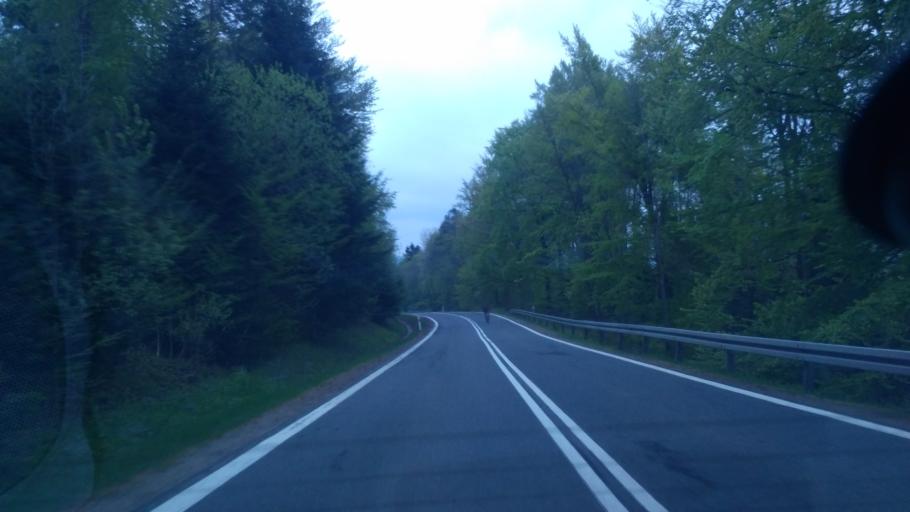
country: PL
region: Subcarpathian Voivodeship
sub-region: Powiat sanocki
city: Tyrawa Woloska
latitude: 49.5586
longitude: 22.3375
